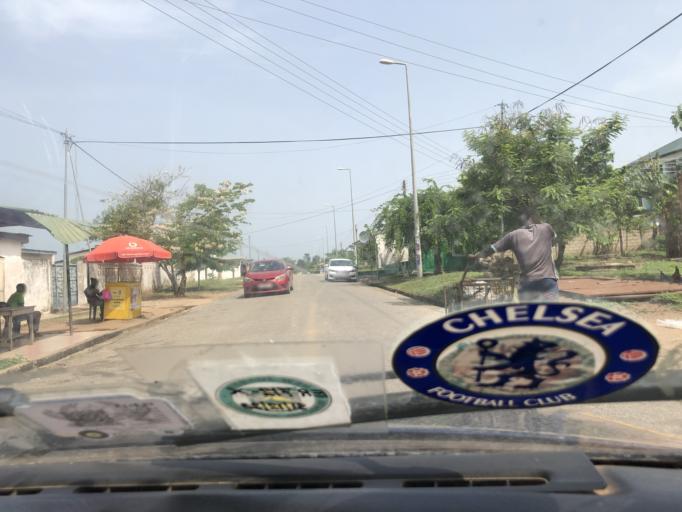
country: GH
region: Eastern
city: Koforidua
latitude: 6.0914
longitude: -0.2729
